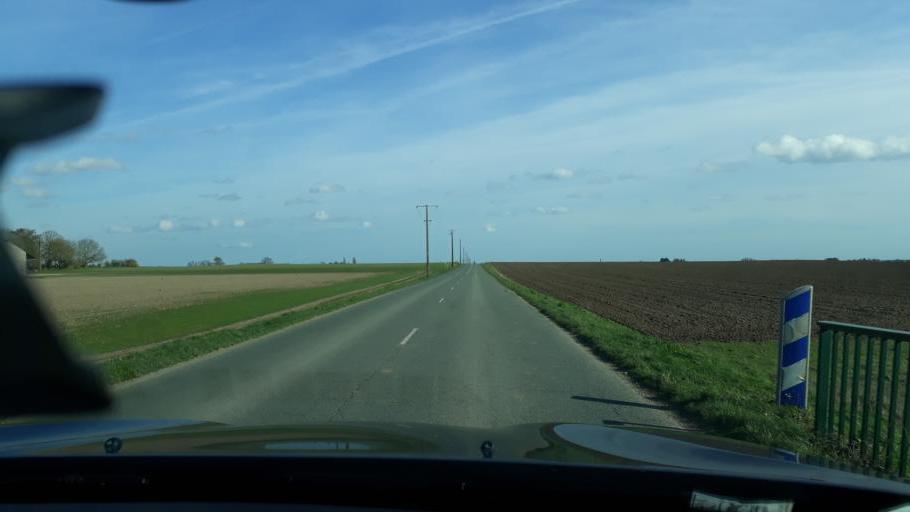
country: FR
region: Centre
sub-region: Departement du Loiret
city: Artenay
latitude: 48.0819
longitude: 1.9213
